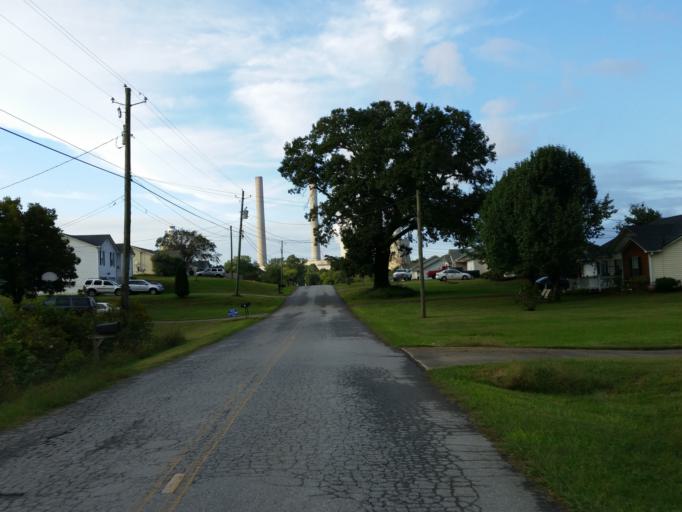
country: US
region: Georgia
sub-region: Bartow County
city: Euharlee
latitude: 34.1091
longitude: -84.9183
